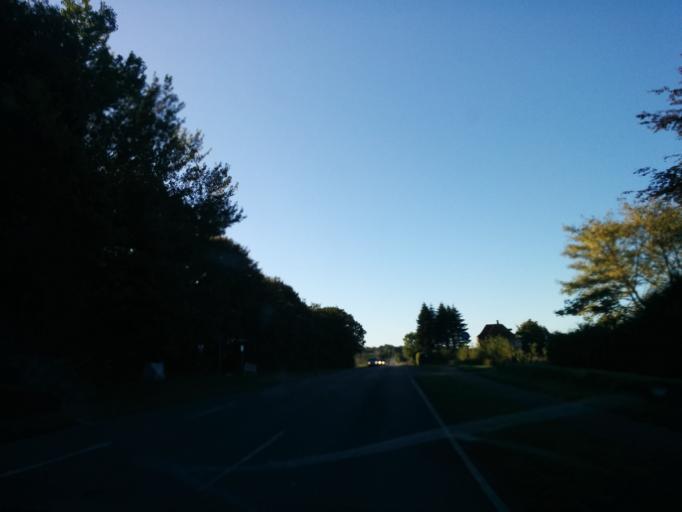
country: DK
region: South Denmark
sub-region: Kolding Kommune
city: Sonder Bjert
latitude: 55.4343
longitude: 9.5608
